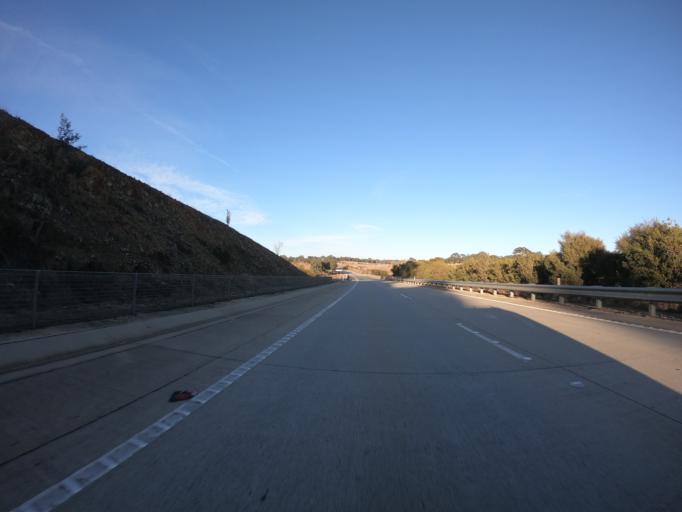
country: AU
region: New South Wales
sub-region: Yass Valley
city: Gundaroo
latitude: -35.1189
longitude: 149.3491
